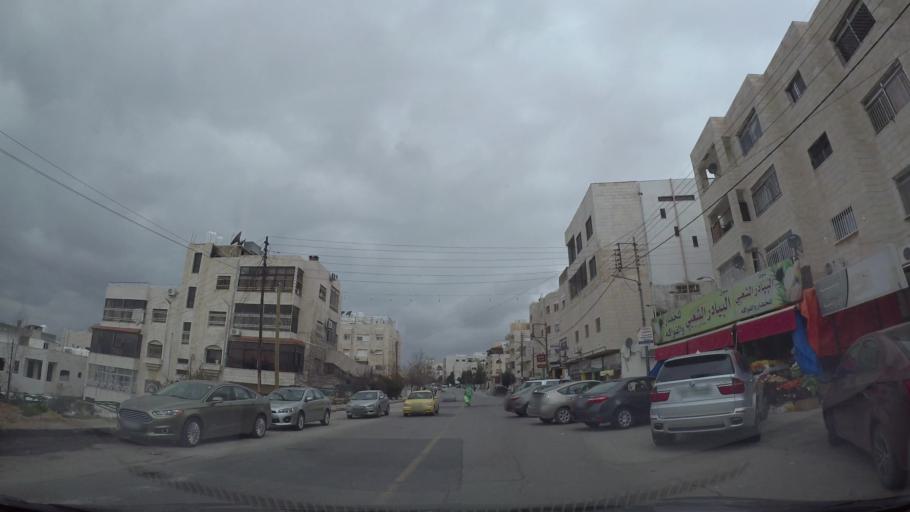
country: JO
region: Amman
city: Wadi as Sir
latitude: 31.9589
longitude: 35.8352
